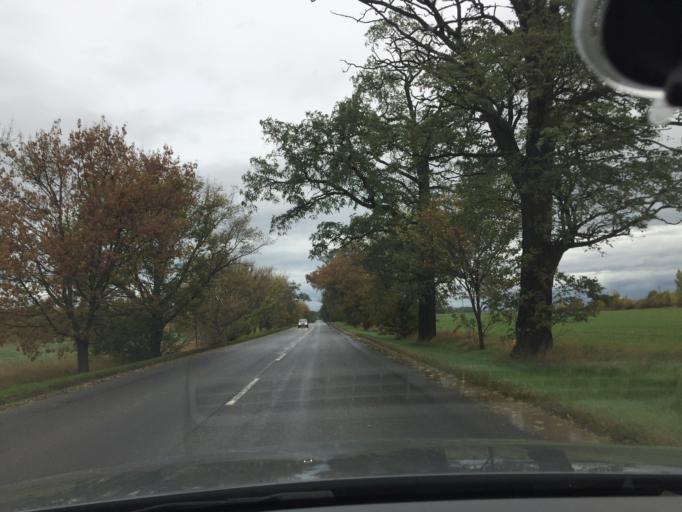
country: CZ
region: Central Bohemia
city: Velvary
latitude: 50.3381
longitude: 14.2812
